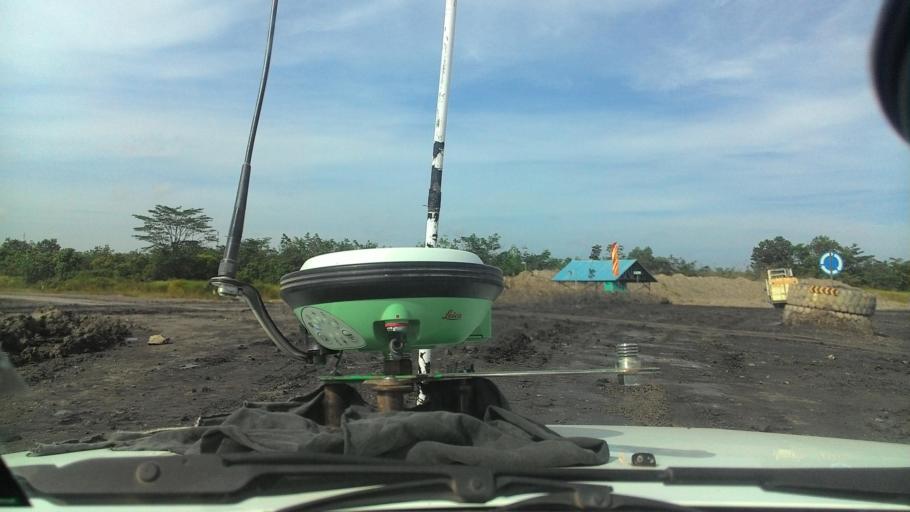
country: ID
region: South Kalimantan
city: Tanta
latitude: -2.1888
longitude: 115.4812
